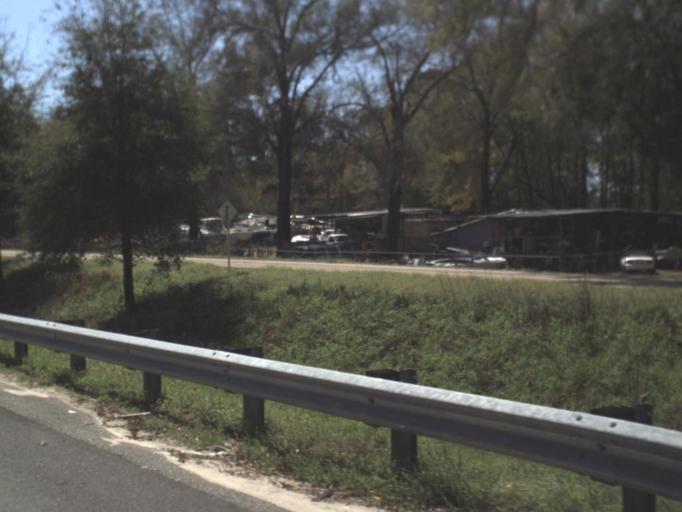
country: US
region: Florida
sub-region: Leon County
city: Tallahassee
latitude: 30.3813
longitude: -84.2727
